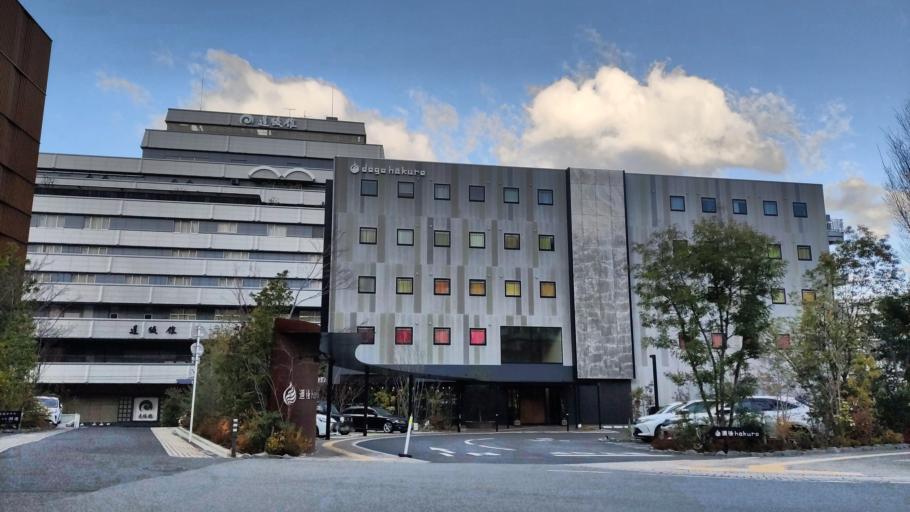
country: JP
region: Ehime
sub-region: Shikoku-chuo Shi
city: Matsuyama
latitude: 33.8536
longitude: 132.7856
